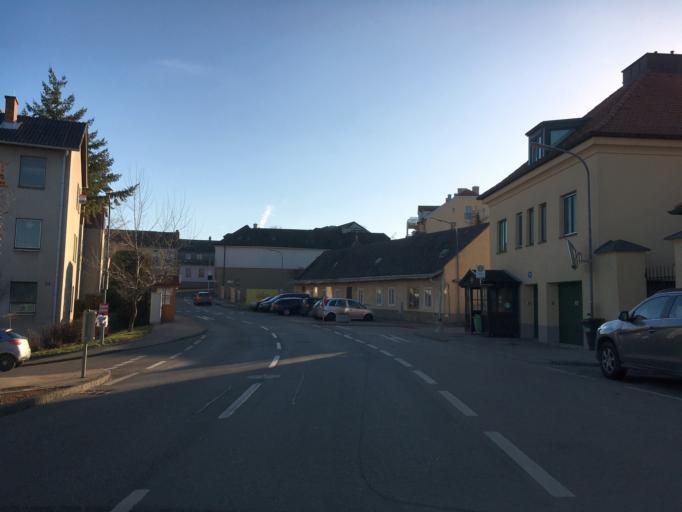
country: AT
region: Lower Austria
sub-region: Politischer Bezirk Wien-Umgebung
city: Klosterneuburg
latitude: 48.3312
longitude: 16.2999
